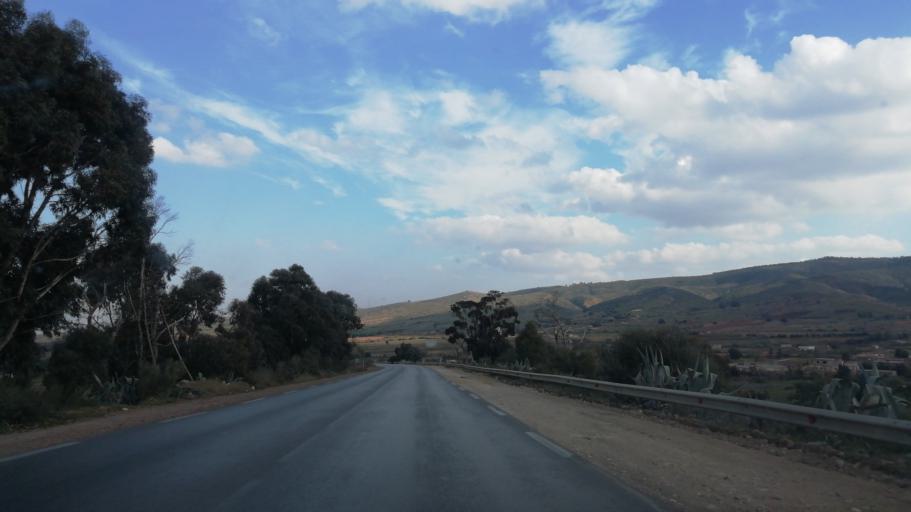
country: DZ
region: Relizane
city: Relizane
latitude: 35.9023
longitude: 0.4472
